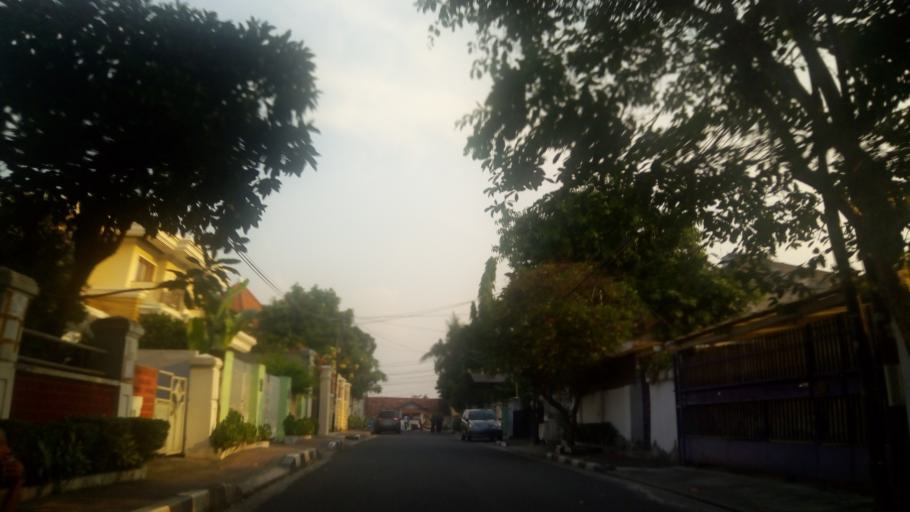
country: ID
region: Jakarta Raya
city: Jakarta
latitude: -6.2047
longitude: 106.8514
